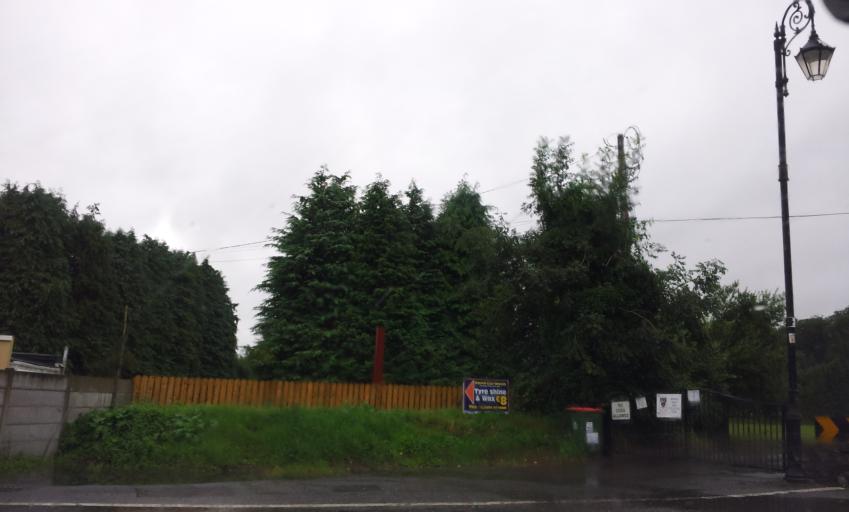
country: IE
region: Munster
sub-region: County Cork
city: Blarney
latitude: 51.9338
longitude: -8.5705
